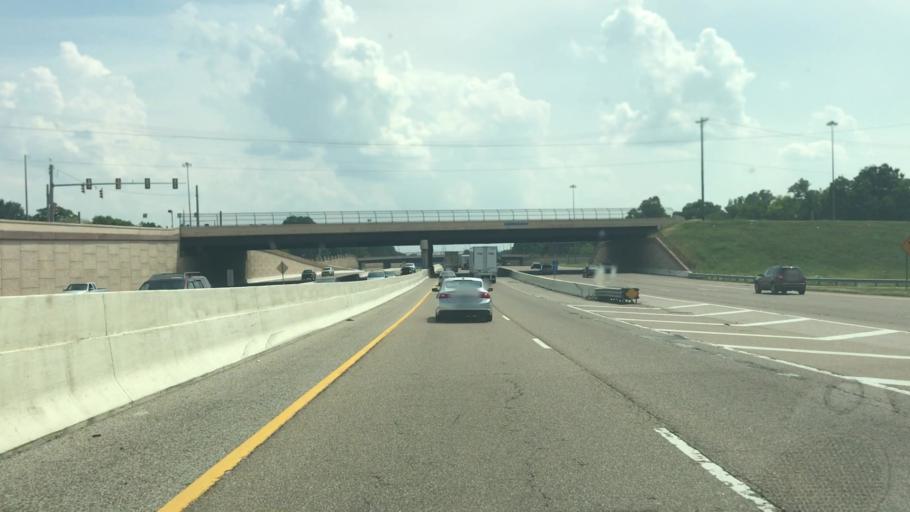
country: US
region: Tennessee
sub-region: Shelby County
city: Memphis
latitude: 35.1593
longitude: -90.0204
